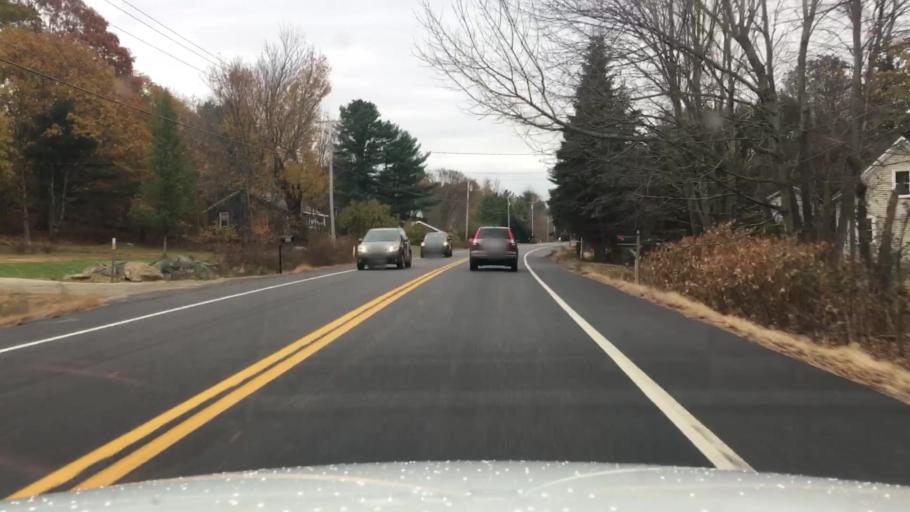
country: US
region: Maine
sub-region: Kennebec County
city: Pittston
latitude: 44.1810
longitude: -69.7462
